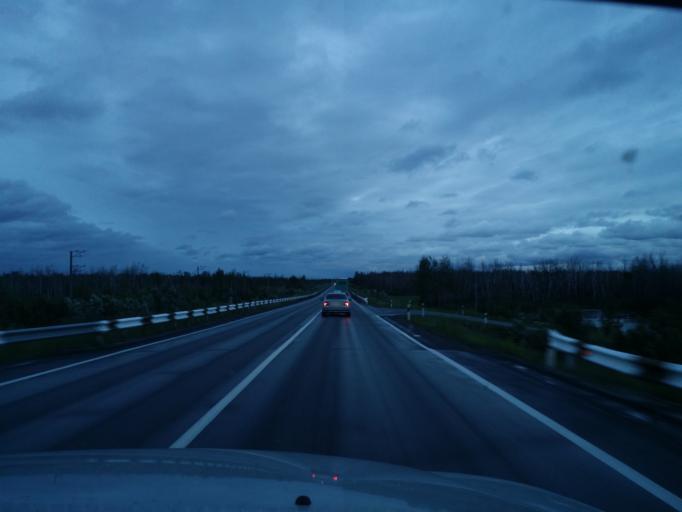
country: RU
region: Khanty-Mansiyskiy Avtonomnyy Okrug
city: Lokosovo
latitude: 61.4556
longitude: 74.6761
